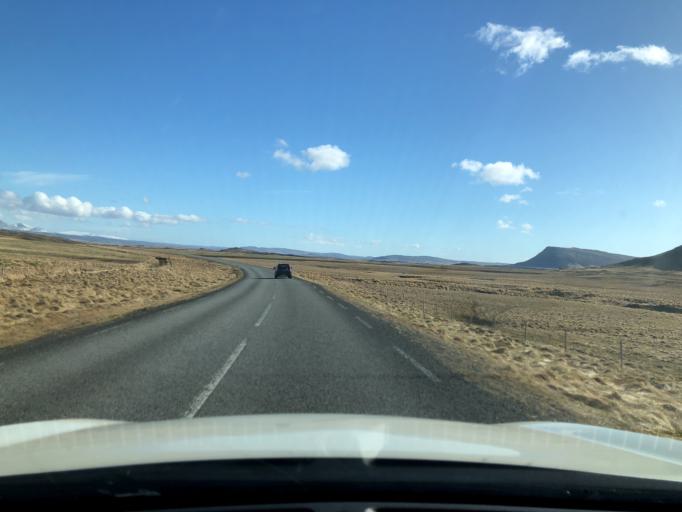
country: IS
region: West
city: Borgarnes
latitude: 64.5733
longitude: -21.6567
